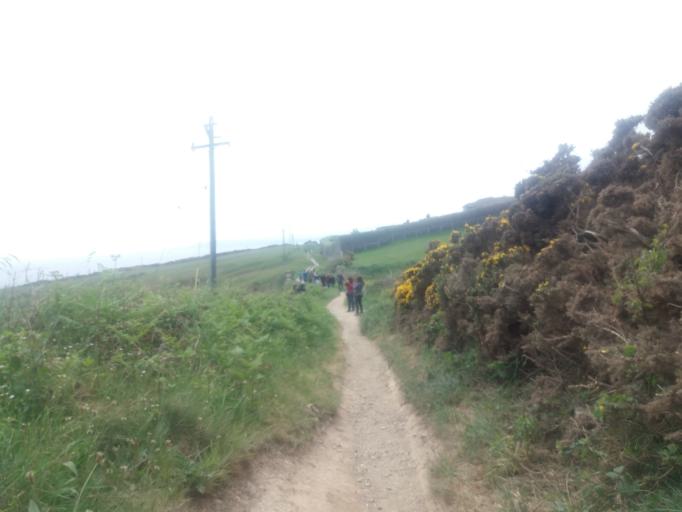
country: IE
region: Leinster
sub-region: Fingal County
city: Howth
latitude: 53.3675
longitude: -6.0555
